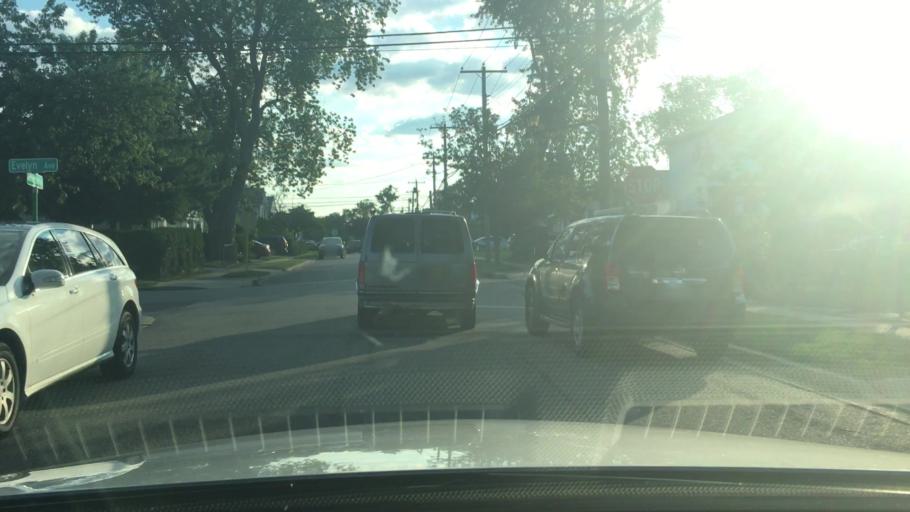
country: US
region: New York
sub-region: Nassau County
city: Westbury
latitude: 40.7487
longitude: -73.5964
